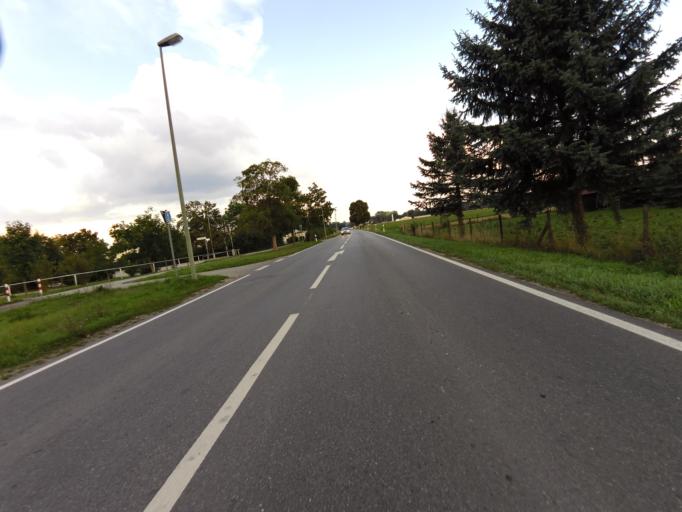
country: DE
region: Bavaria
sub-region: Upper Bavaria
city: Moosburg
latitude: 48.4649
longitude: 11.9598
